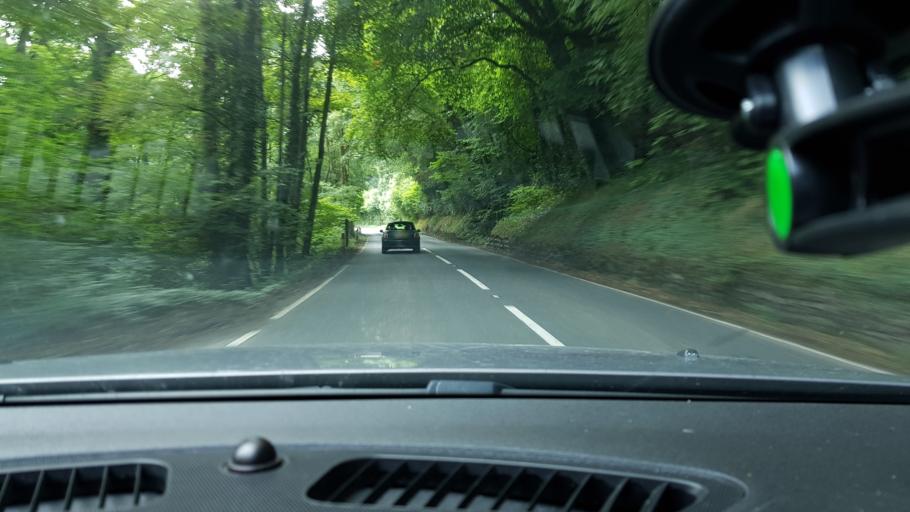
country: GB
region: England
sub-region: Cornwall
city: Helland
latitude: 50.5646
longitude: -4.7537
